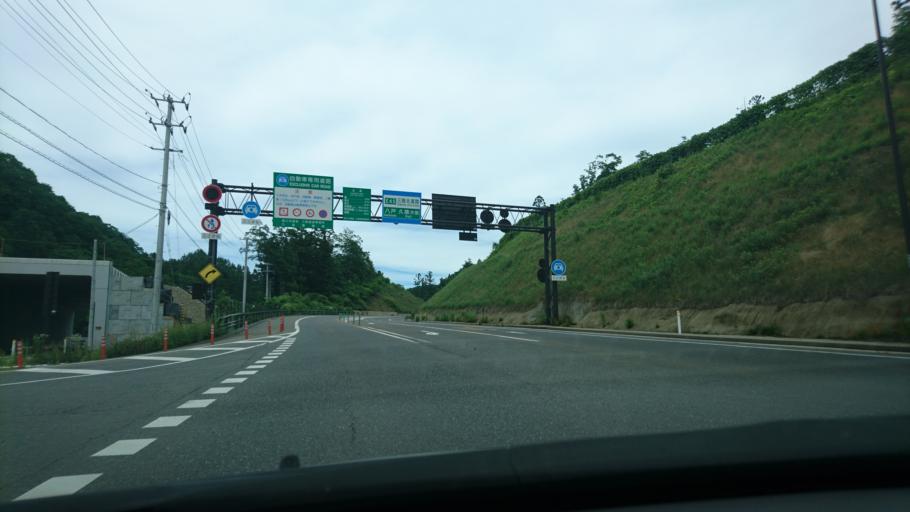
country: JP
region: Iwate
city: Miyako
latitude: 39.9919
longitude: 141.8791
